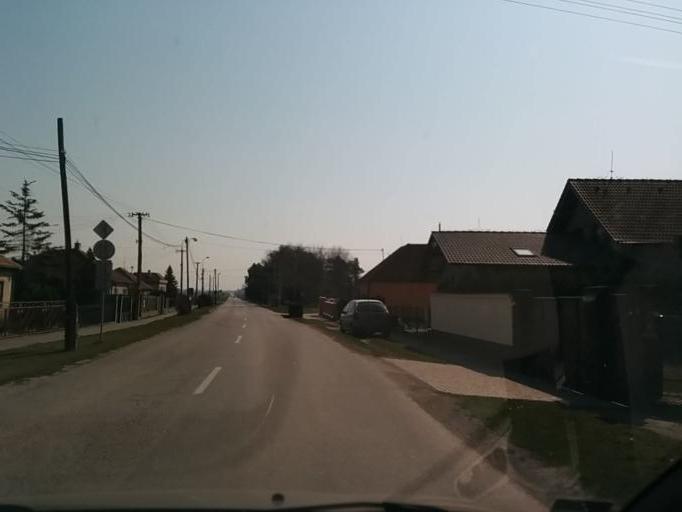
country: SK
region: Trnavsky
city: Sladkovicovo
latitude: 48.2270
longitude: 17.5771
